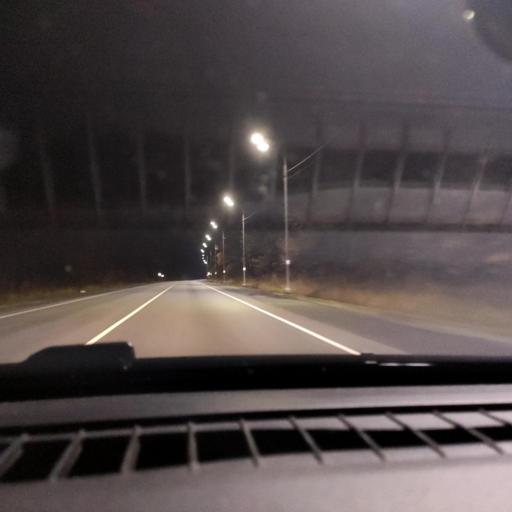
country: RU
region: Voronezj
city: Semiluki
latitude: 51.6384
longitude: 39.0079
